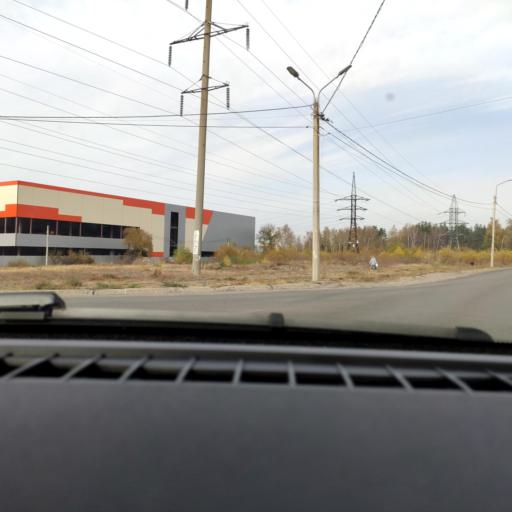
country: RU
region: Voronezj
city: Maslovka
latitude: 51.5949
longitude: 39.2485
